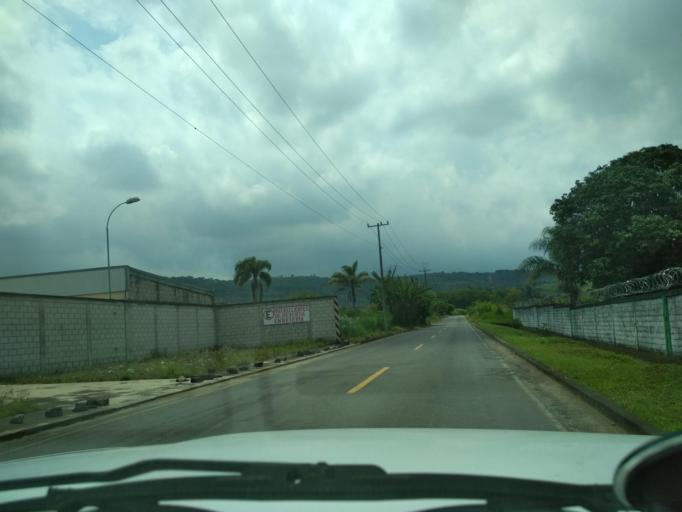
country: MX
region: Veracruz
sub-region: Ixtaczoquitlan
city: Buenavista
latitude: 18.8913
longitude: -97.0496
